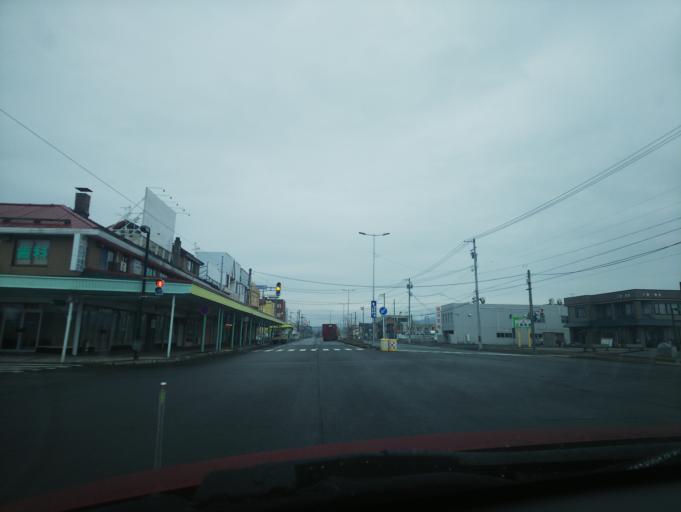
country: JP
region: Hokkaido
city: Nayoro
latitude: 44.3492
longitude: 142.4638
